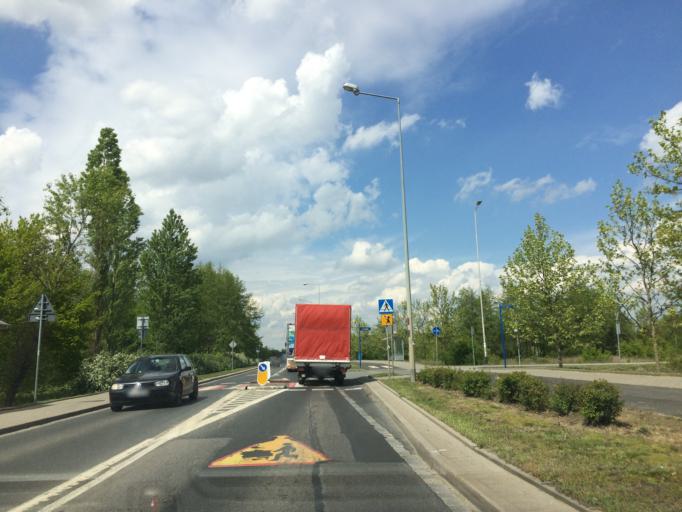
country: PL
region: Lower Silesian Voivodeship
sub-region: Powiat wroclawski
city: Smolec
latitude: 51.1517
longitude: 16.9273
